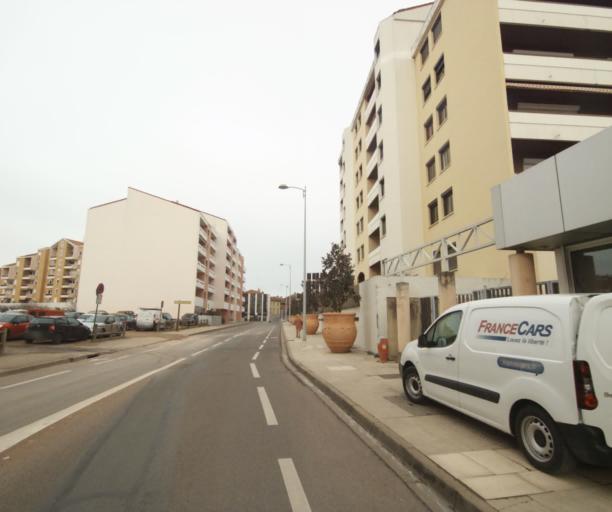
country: FR
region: Rhone-Alpes
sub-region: Departement de la Loire
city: Roanne
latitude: 46.0330
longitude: 4.0716
